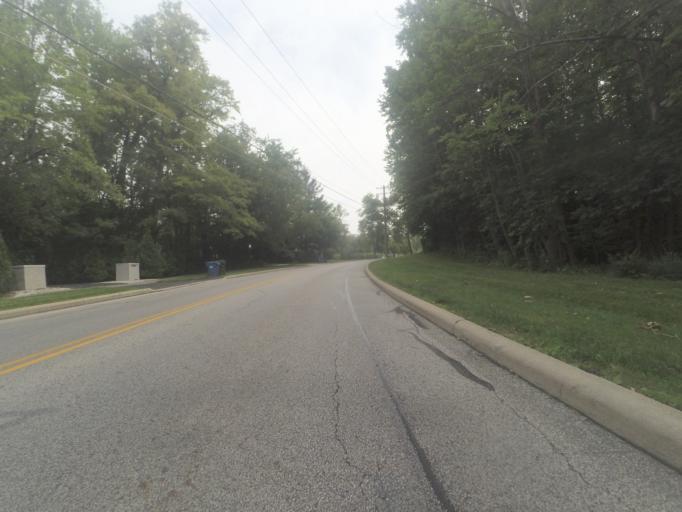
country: US
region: Ohio
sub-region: Cuyahoga County
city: Bratenahl
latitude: 41.5585
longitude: -81.6000
